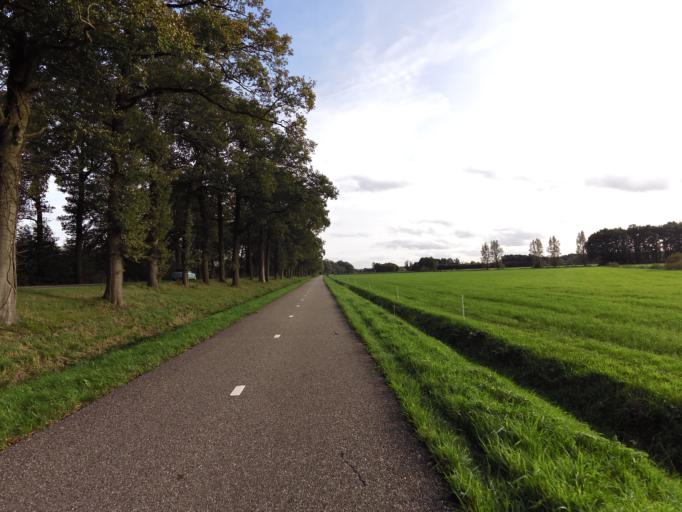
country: NL
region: Gelderland
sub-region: Gemeente Bronckhorst
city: Baak
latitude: 52.0204
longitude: 6.2219
